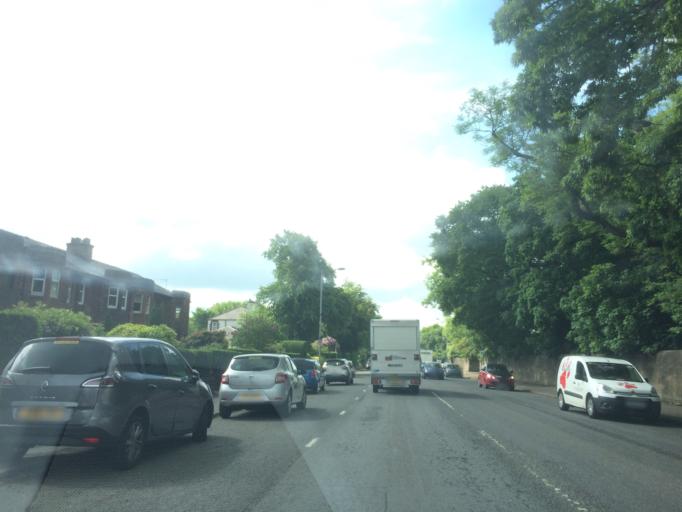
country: GB
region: Scotland
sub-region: East Renfrewshire
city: Giffnock
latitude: 55.8310
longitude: -4.2958
